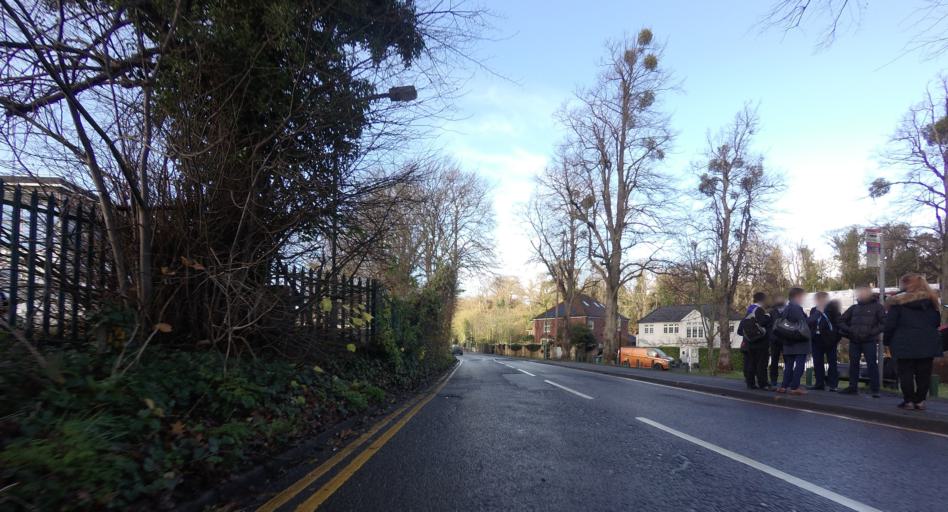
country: GB
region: England
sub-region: Kent
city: Dartford
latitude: 51.4287
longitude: 0.1948
